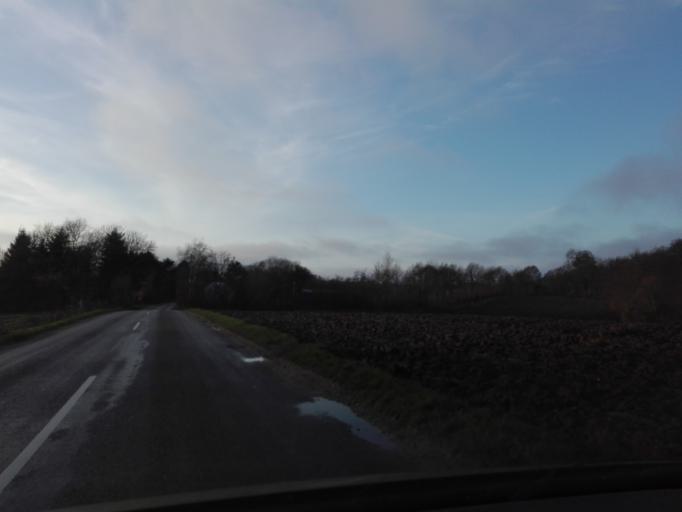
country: DK
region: Central Jutland
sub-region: Arhus Kommune
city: Malling
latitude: 56.0395
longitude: 10.1809
